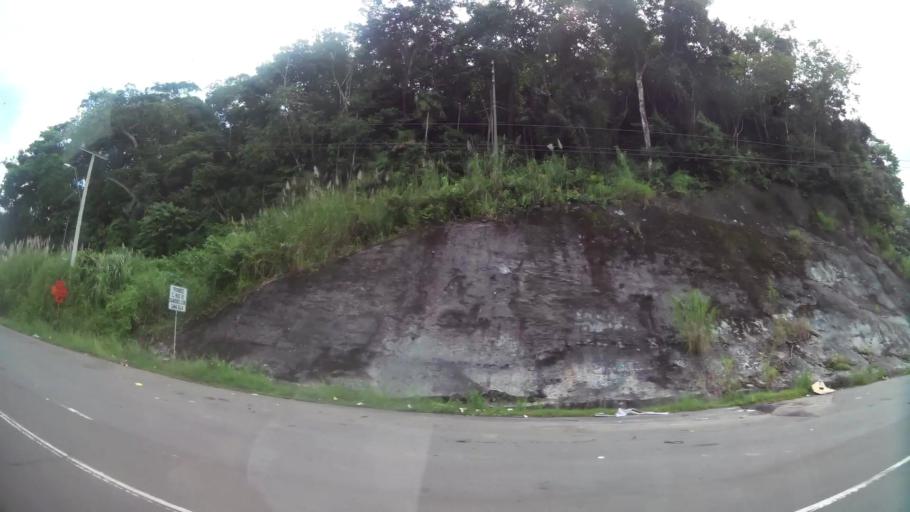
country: PA
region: Panama
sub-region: Distrito de Panama
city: Paraiso
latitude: 9.0349
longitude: -79.6314
